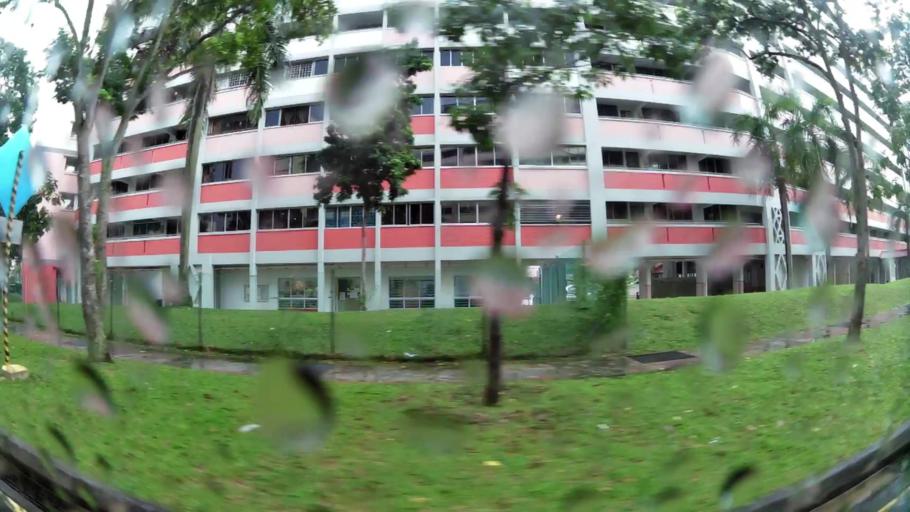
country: SG
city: Singapore
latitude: 1.3444
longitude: 103.9562
